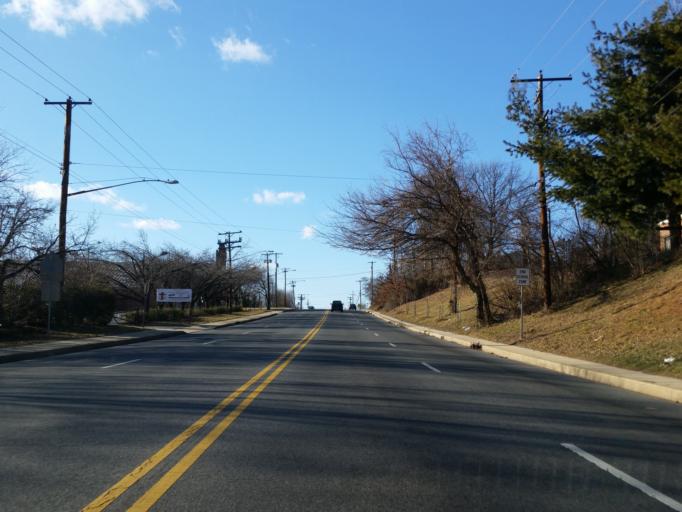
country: US
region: Maryland
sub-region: Prince George's County
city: Chillum
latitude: 38.9567
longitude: -76.9836
